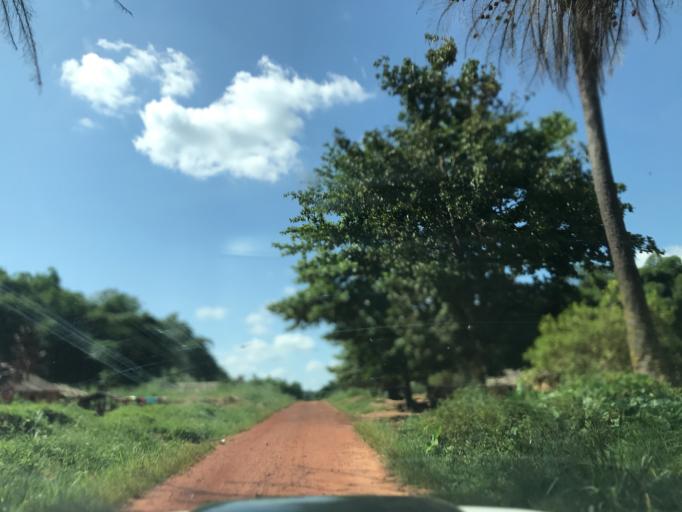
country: CD
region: Eastern Province
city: Kisangani
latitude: 1.2426
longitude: 25.2724
